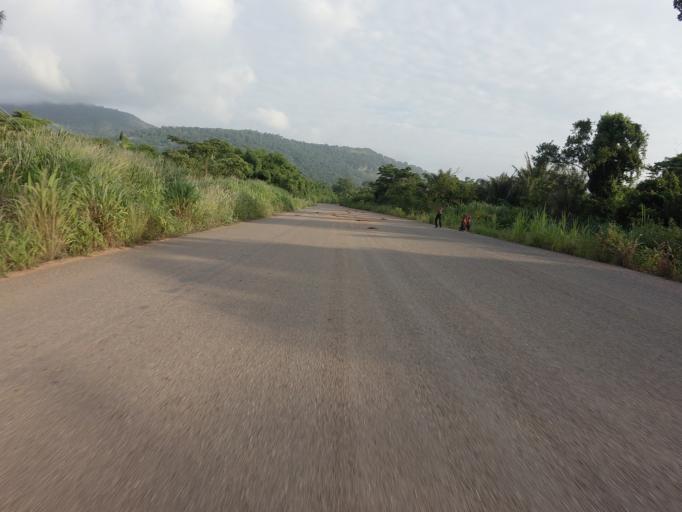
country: TG
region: Plateaux
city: Kpalime
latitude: 6.9333
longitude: 0.4628
